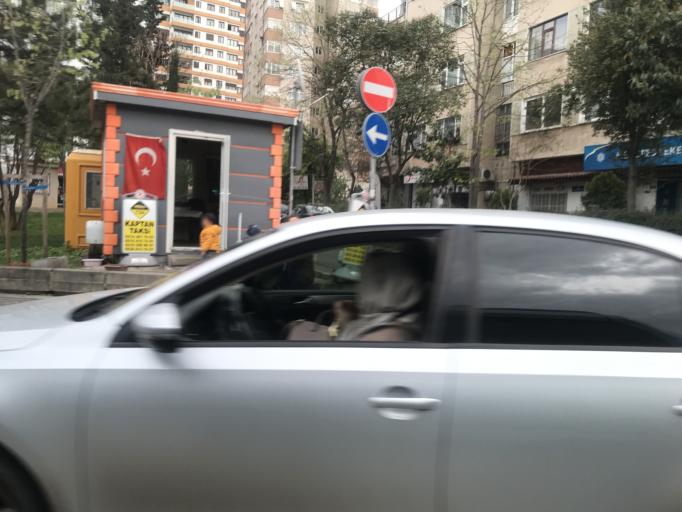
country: TR
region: Istanbul
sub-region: Atasehir
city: Atasehir
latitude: 40.9703
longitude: 29.0843
